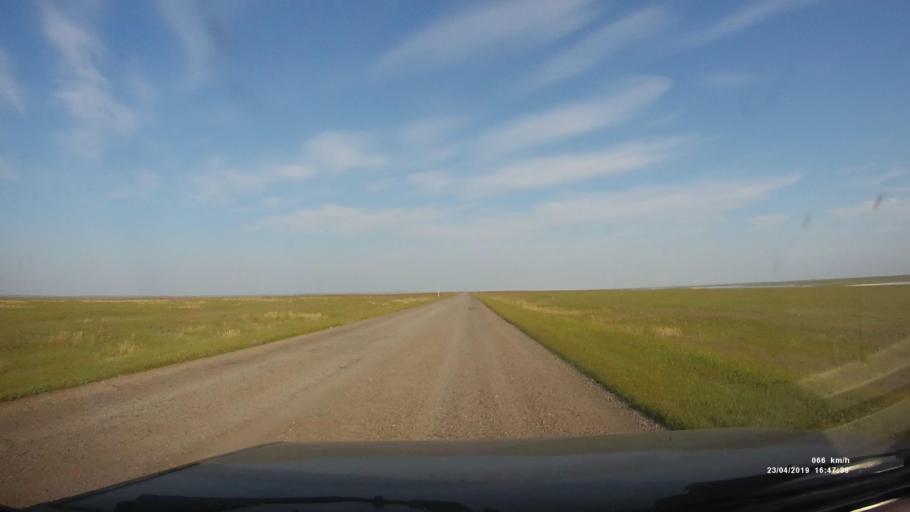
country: RU
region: Kalmykiya
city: Priyutnoye
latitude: 46.3380
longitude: 43.2506
